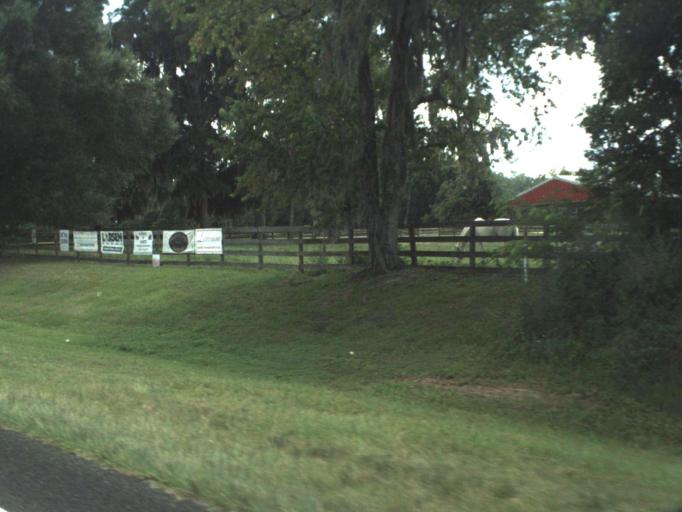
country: US
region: Florida
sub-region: Marion County
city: Citra
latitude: 29.3345
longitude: -82.1518
